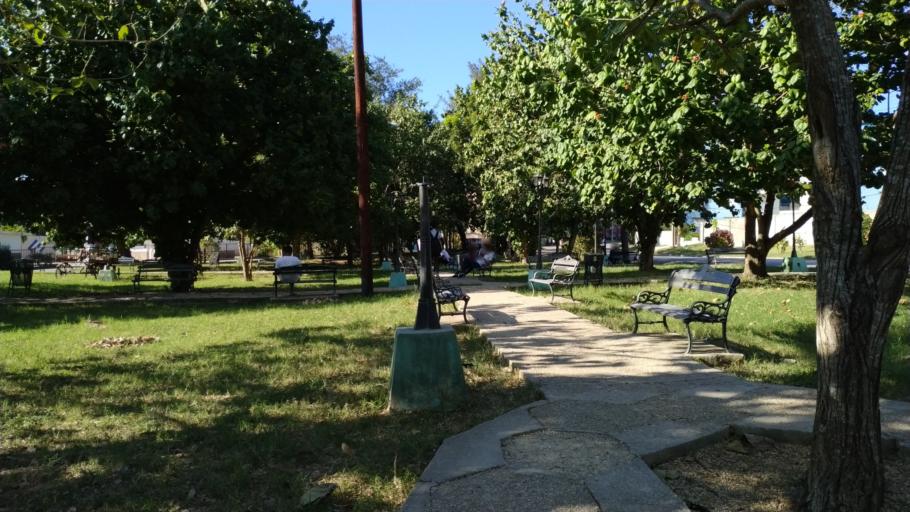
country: CU
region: La Habana
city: Arroyo Naranjo
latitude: 23.0573
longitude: -82.3916
